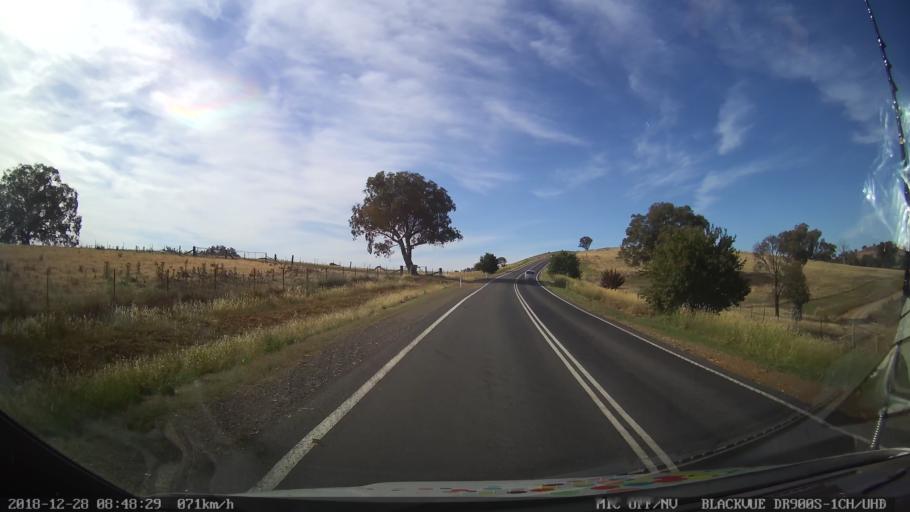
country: AU
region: New South Wales
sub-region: Upper Lachlan Shire
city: Crookwell
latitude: -34.0373
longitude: 149.3367
